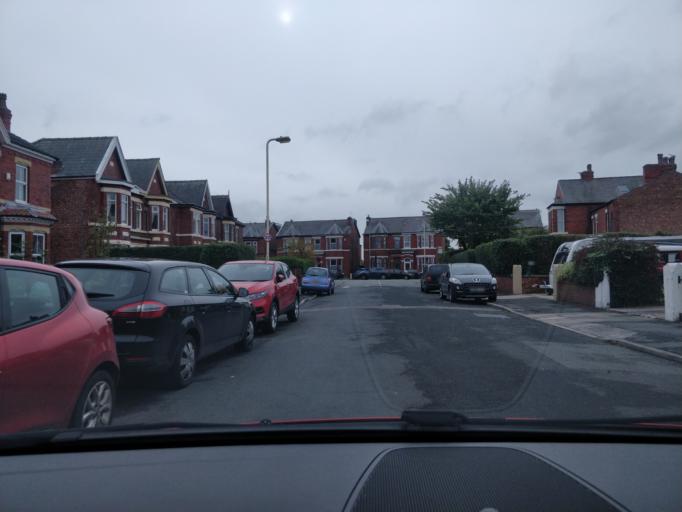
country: GB
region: England
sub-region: Sefton
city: Southport
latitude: 53.6358
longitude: -2.9937
